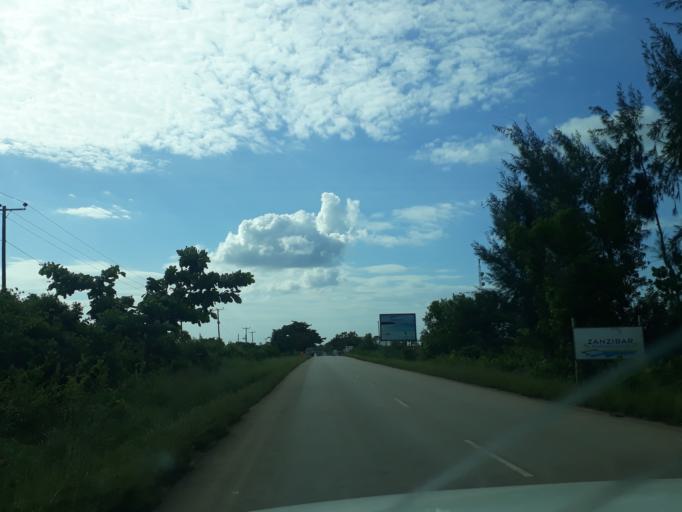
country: TZ
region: Zanzibar North
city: Nungwi
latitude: -5.7590
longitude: 39.3016
